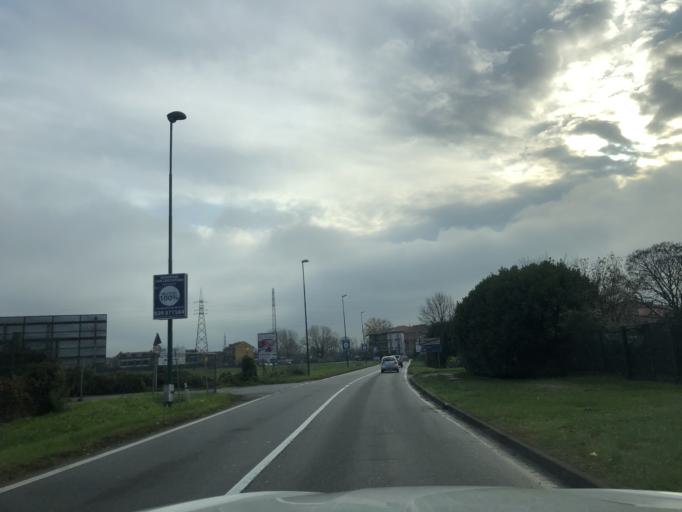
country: IT
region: Lombardy
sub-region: Citta metropolitana di Milano
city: Cologno Monzese
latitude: 45.5496
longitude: 9.2711
